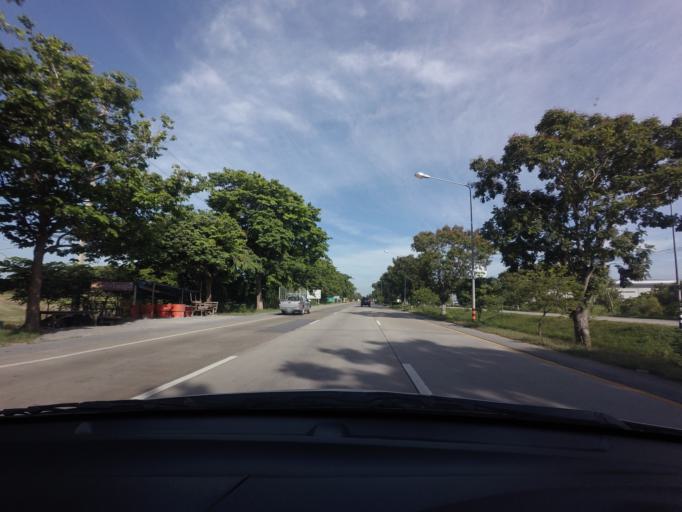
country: TH
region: Suphan Buri
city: Bang Pla Ma
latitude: 14.4309
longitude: 100.1435
